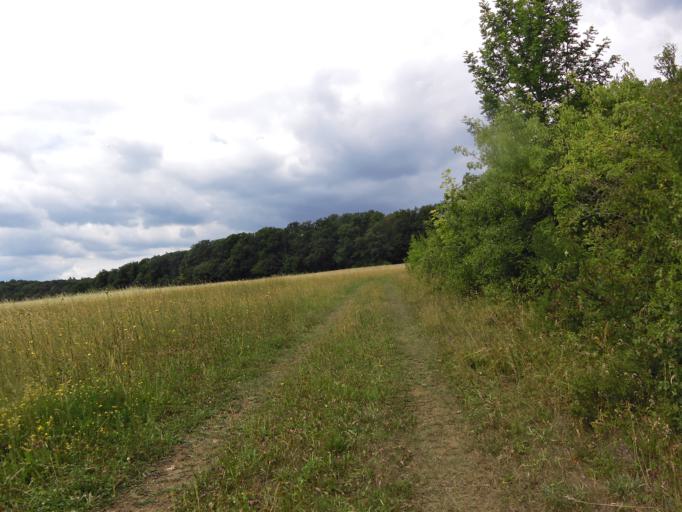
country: DE
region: Bavaria
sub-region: Regierungsbezirk Unterfranken
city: Reichenberg
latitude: 49.7617
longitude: 9.9209
